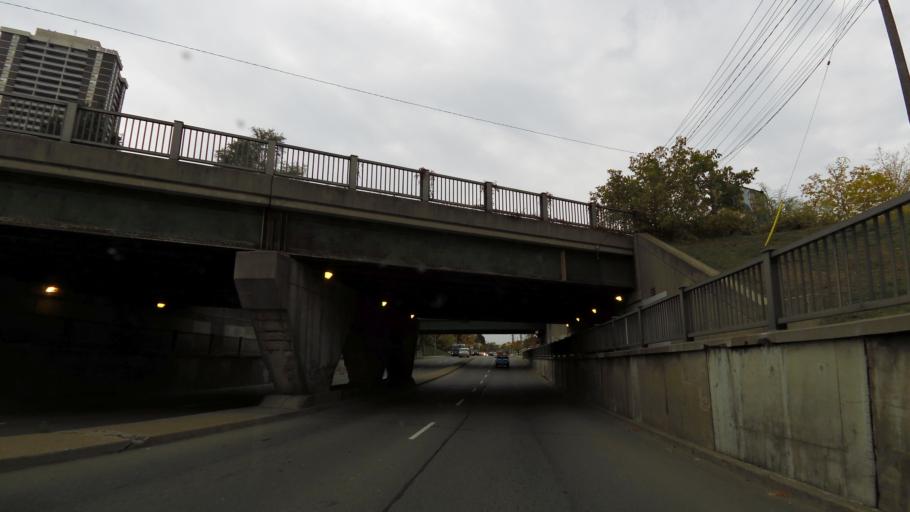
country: CA
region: Ontario
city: Etobicoke
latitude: 43.6462
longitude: -79.5242
